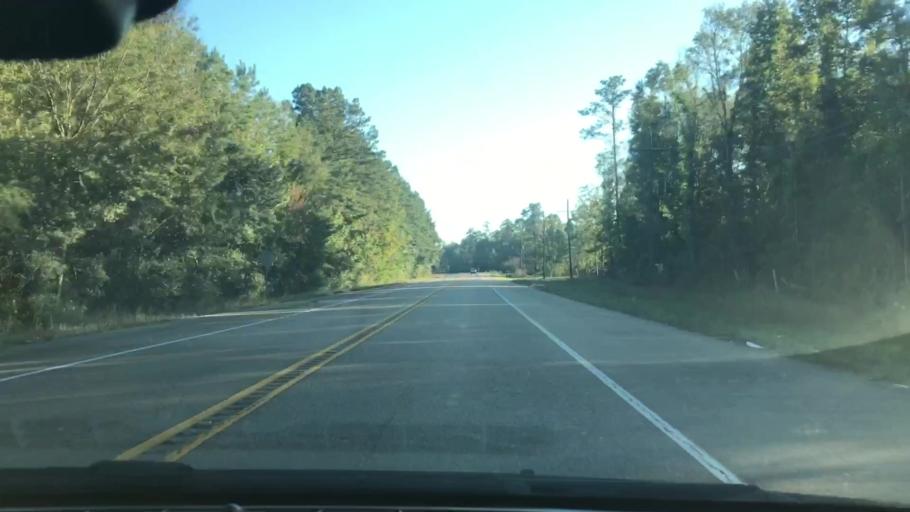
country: US
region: Louisiana
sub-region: Washington Parish
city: Bogalusa
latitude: 30.6027
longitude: -89.8727
